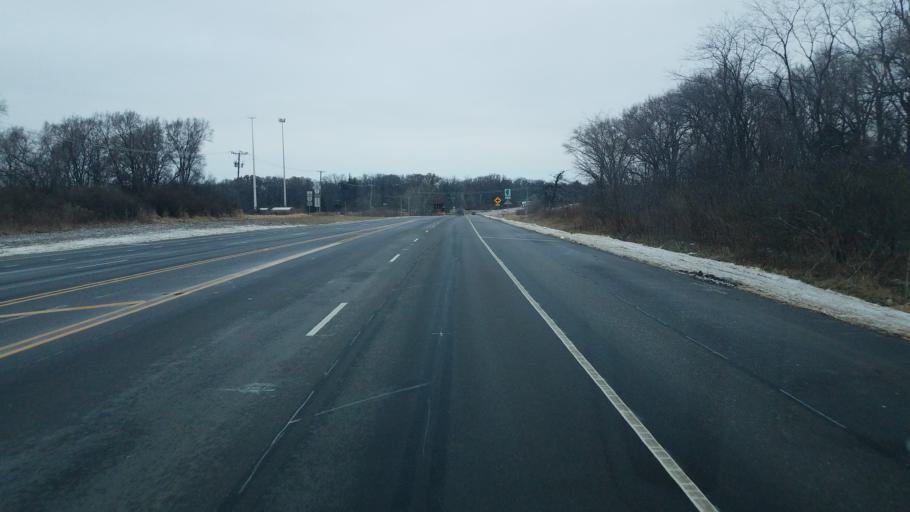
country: US
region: Illinois
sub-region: Kane County
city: Sugar Grove
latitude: 41.8205
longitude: -88.4670
